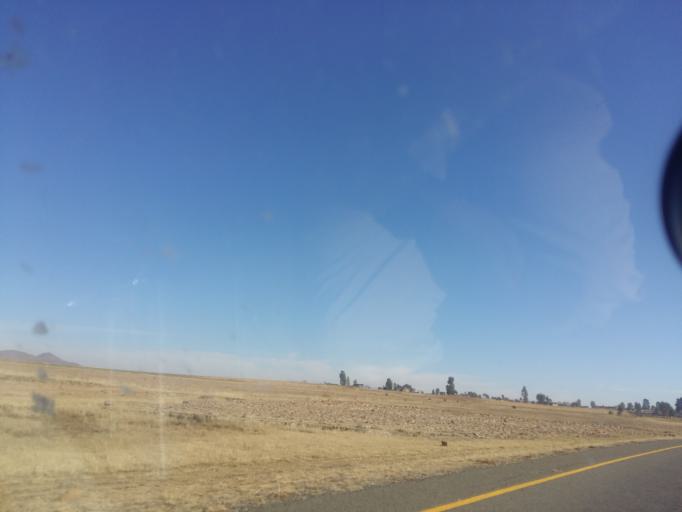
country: LS
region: Mafeteng
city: Mafeteng
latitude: -29.6656
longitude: 27.2733
